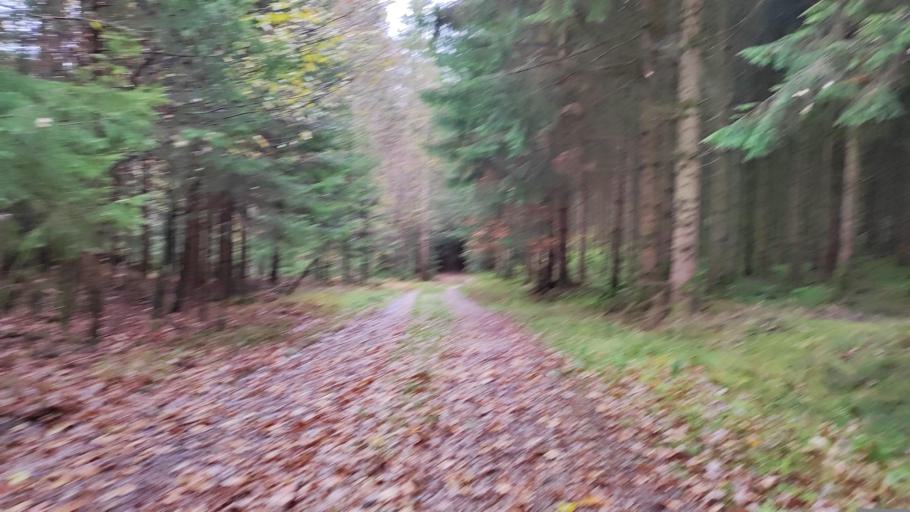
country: DE
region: Bavaria
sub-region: Swabia
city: Dinkelscherben
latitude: 48.3547
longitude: 10.5280
